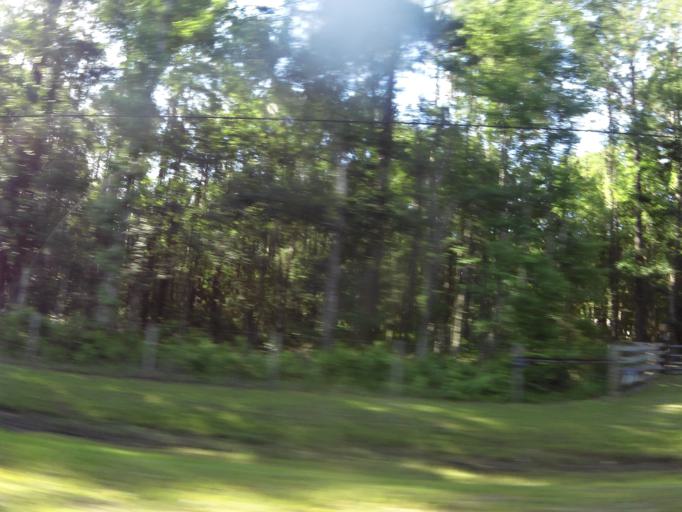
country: US
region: Florida
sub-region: Nassau County
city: Nassau Village-Ratliff
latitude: 30.4874
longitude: -81.8358
